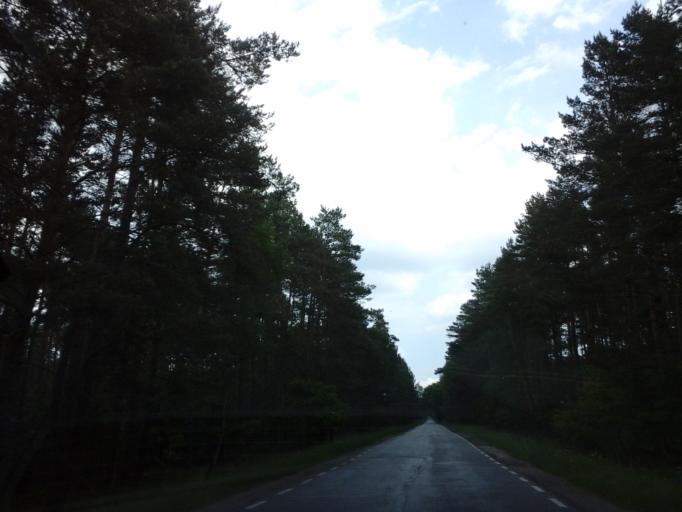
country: PL
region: West Pomeranian Voivodeship
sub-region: Powiat choszczenski
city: Drawno
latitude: 53.2446
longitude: 15.8262
